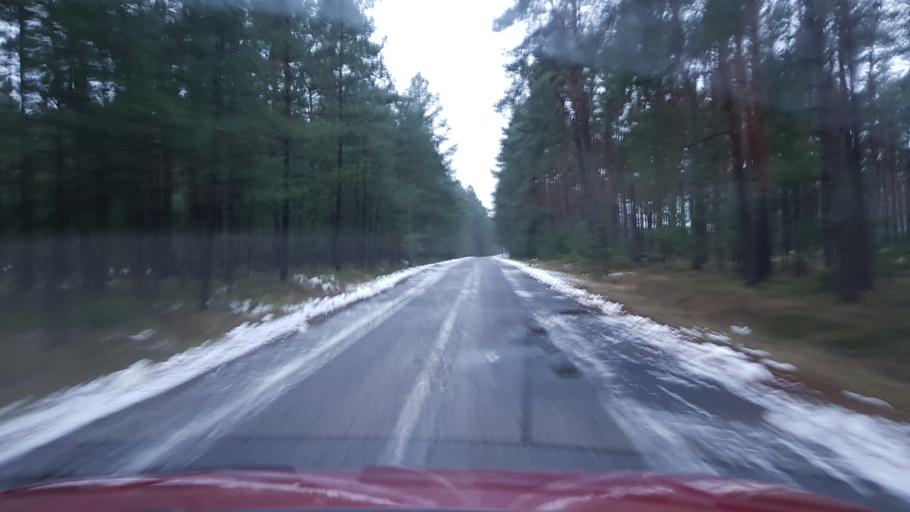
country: PL
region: West Pomeranian Voivodeship
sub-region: Powiat goleniowski
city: Goleniow
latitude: 53.4838
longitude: 14.8506
